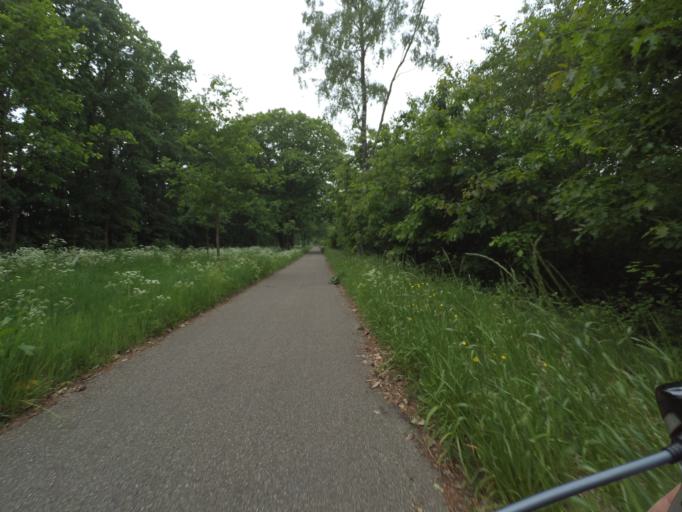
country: NL
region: Gelderland
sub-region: Gemeente Renkum
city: Wolfheze
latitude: 52.0089
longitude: 5.7724
